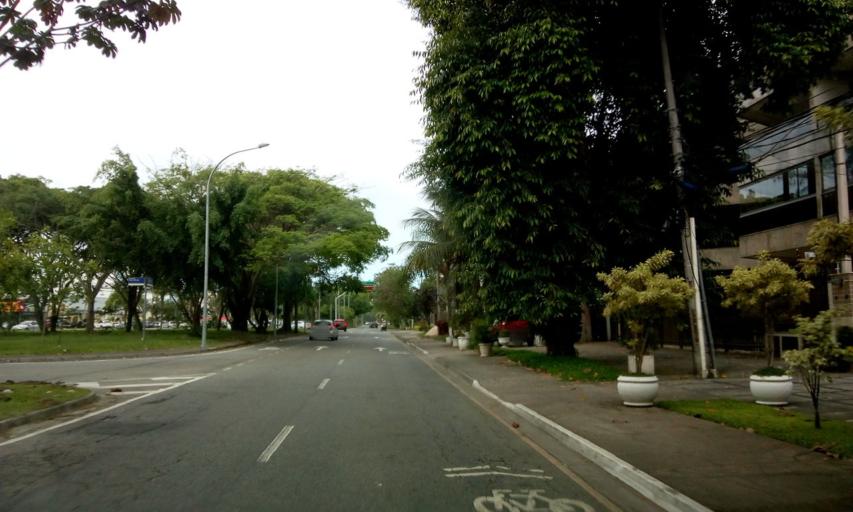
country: BR
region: Rio de Janeiro
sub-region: Nilopolis
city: Nilopolis
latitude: -23.0177
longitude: -43.4505
